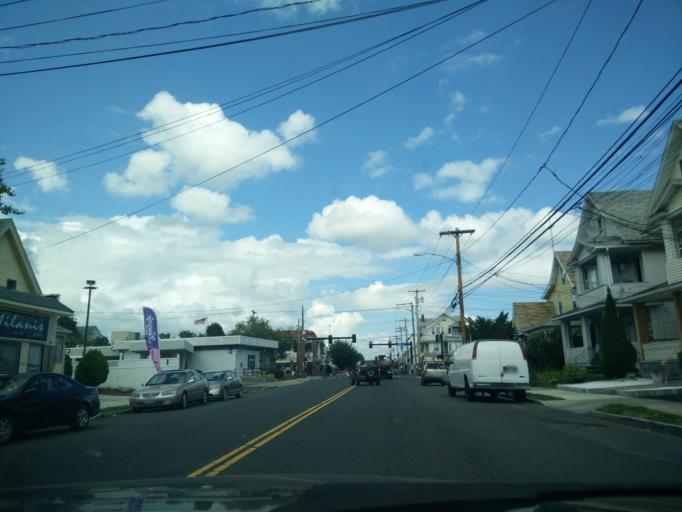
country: US
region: Connecticut
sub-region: Fairfield County
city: Bridgeport
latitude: 41.1936
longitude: -73.2068
